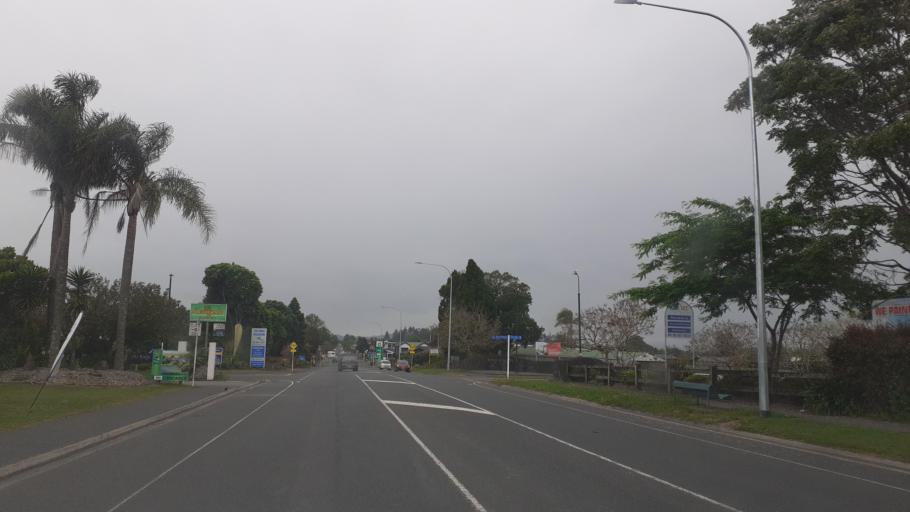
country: NZ
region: Northland
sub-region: Far North District
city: Kerikeri
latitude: -35.2326
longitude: 173.9444
